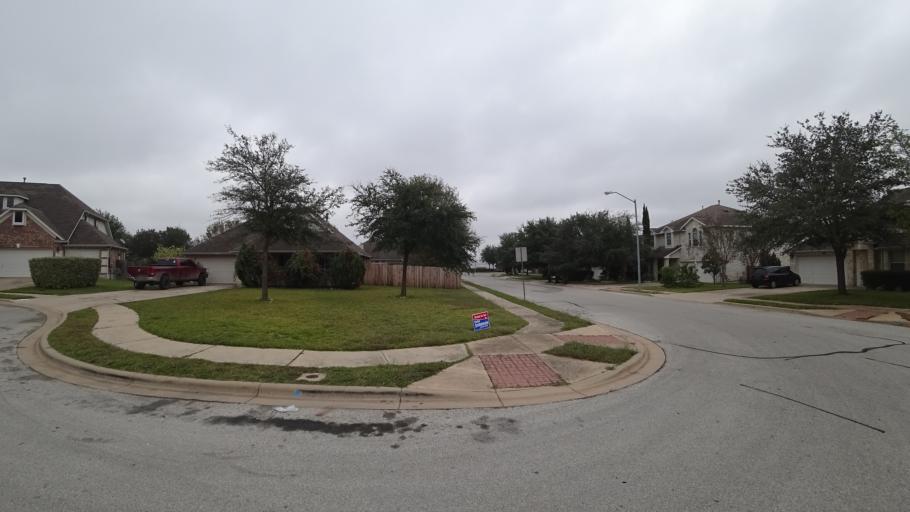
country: US
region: Texas
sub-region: Travis County
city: Pflugerville
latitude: 30.4263
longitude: -97.6180
